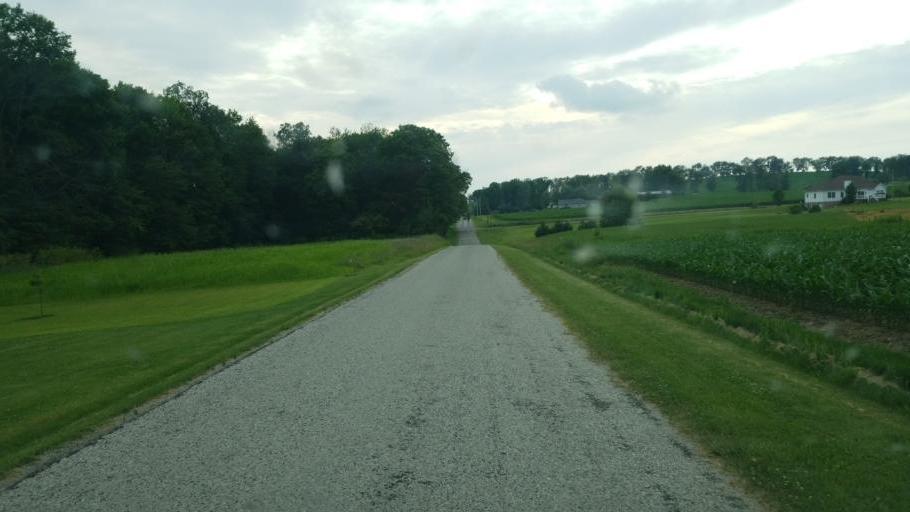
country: US
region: Ohio
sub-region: Wayne County
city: Shreve
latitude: 40.7775
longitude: -82.1241
